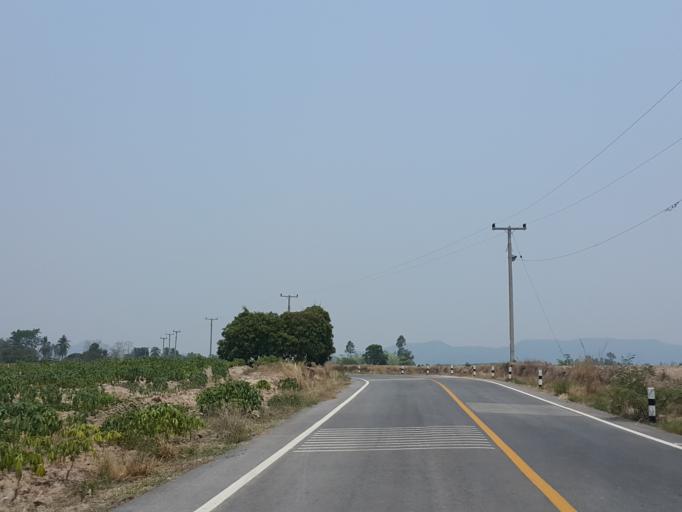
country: TH
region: Kamphaeng Phet
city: Khlong Lan
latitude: 16.0580
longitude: 99.3354
